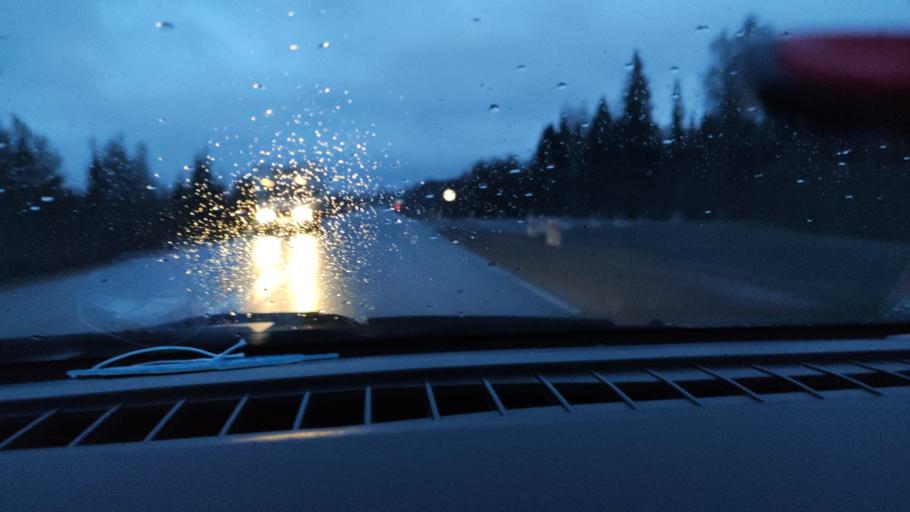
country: RU
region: Udmurtiya
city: Mozhga
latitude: 56.3252
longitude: 52.3163
